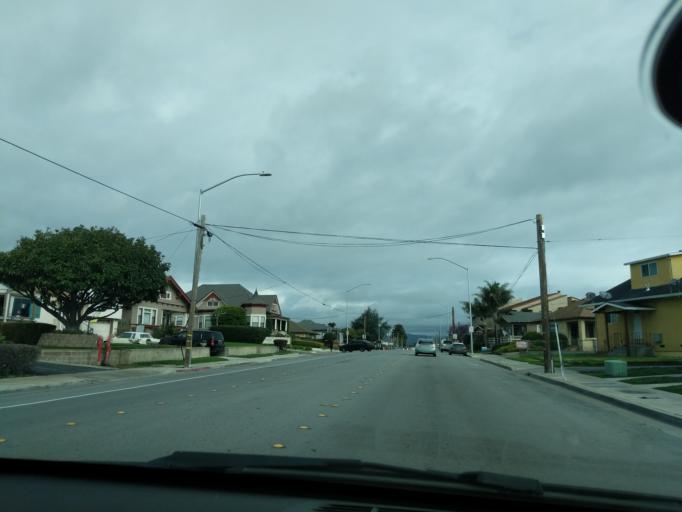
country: US
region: California
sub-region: Santa Cruz County
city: Watsonville
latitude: 36.9192
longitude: -121.7603
